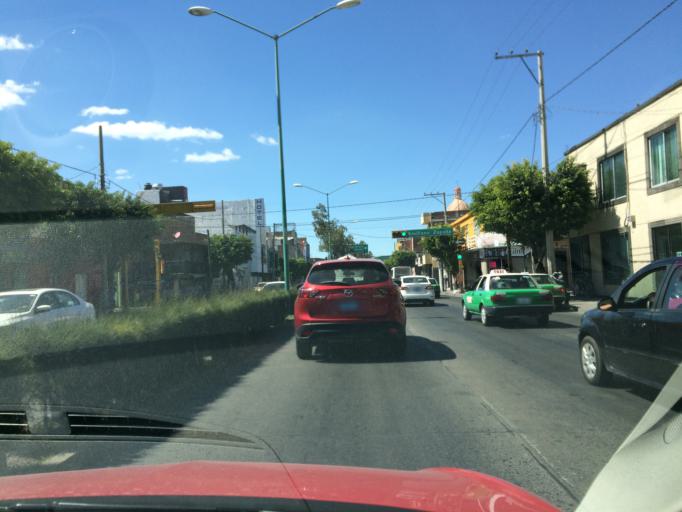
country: MX
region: Guanajuato
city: Leon
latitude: 21.1150
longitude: -101.6832
